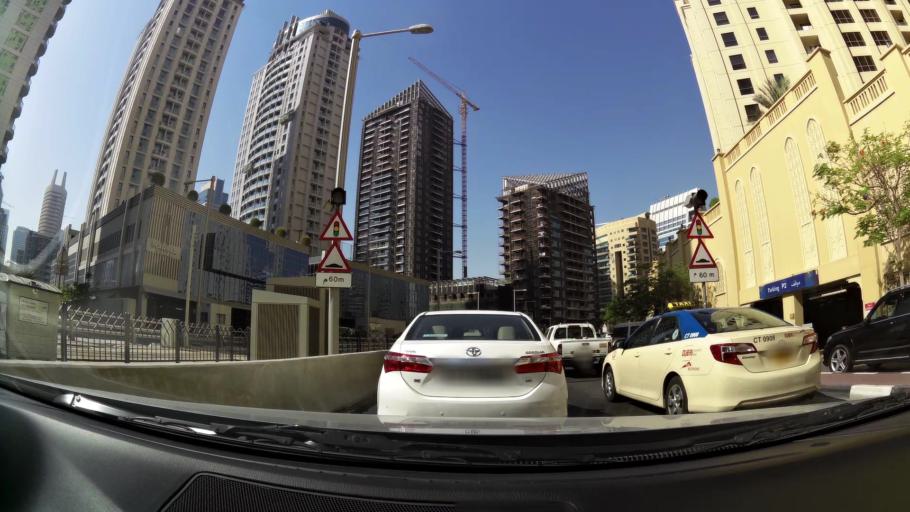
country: AE
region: Dubai
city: Dubai
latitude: 25.0735
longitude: 55.1322
